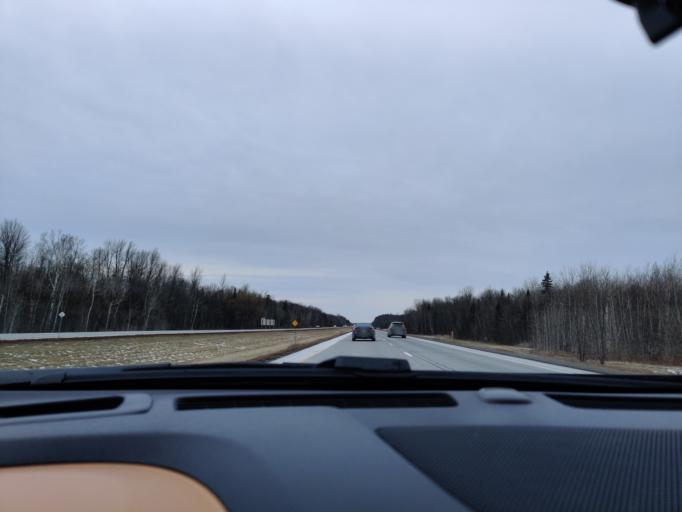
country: US
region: New York
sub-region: St. Lawrence County
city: Ogdensburg
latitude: 44.7959
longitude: -75.4292
